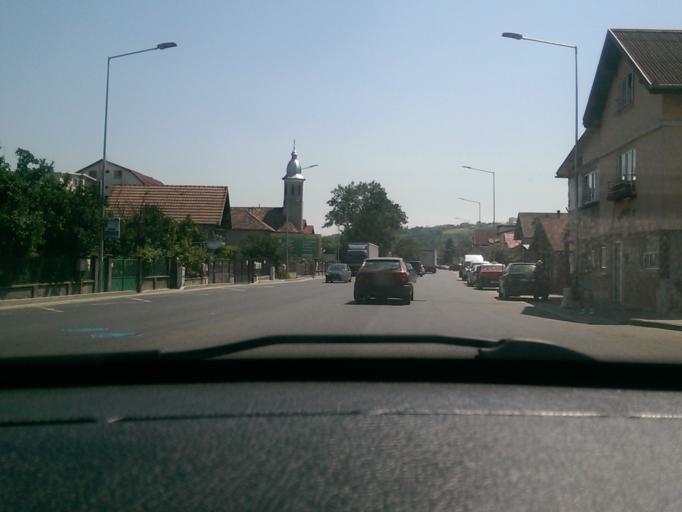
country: RO
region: Cluj
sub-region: Comuna Baciu
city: Baciu
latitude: 46.7846
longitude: 23.5551
